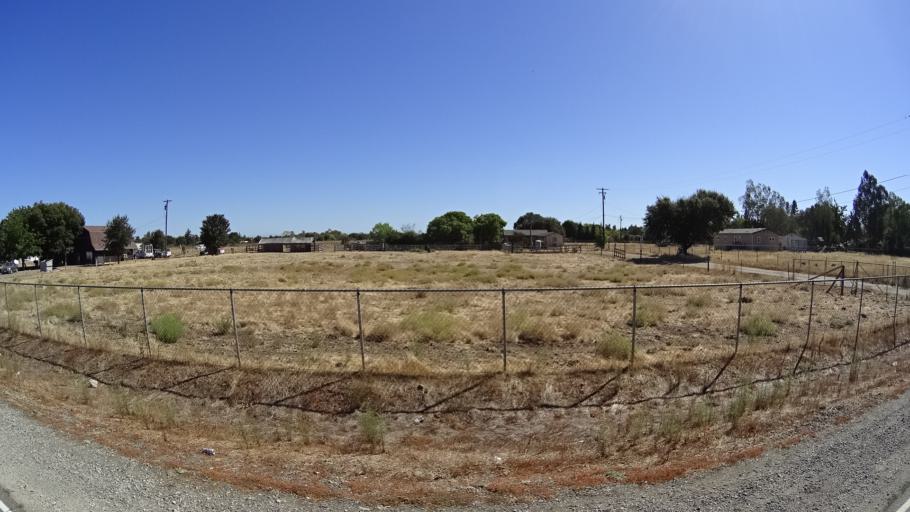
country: US
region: California
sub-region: Sacramento County
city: Vineyard
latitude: 38.4399
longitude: -121.3253
